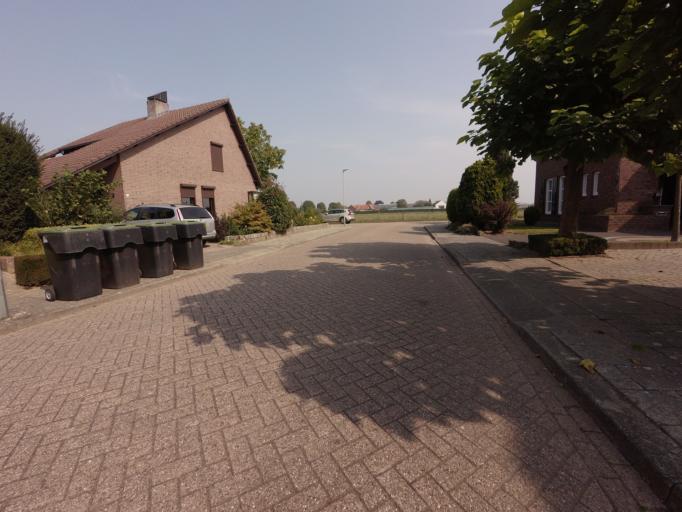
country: BE
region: Flanders
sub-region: Provincie Limburg
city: Maaseik
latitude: 51.0852
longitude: 5.8184
